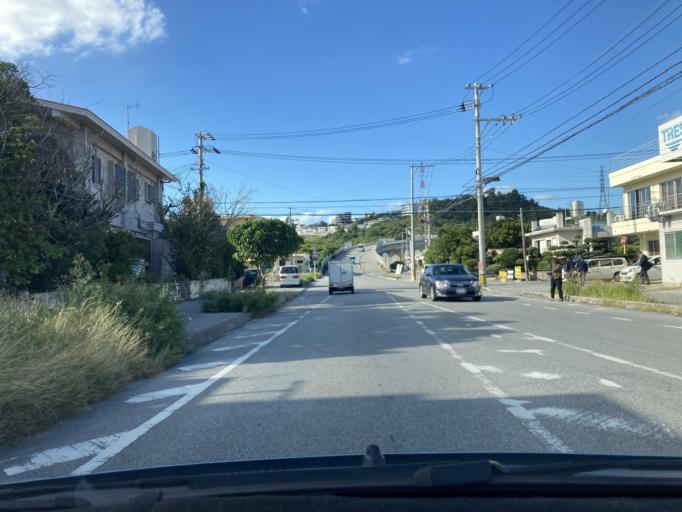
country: JP
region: Okinawa
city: Okinawa
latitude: 26.3356
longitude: 127.8365
